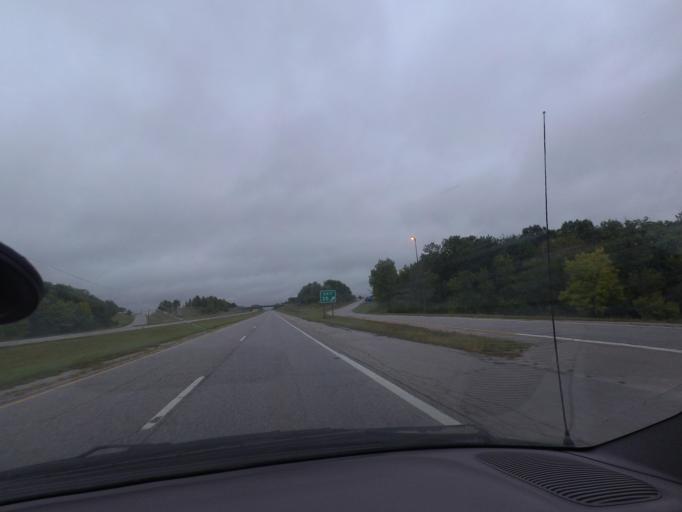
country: US
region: Illinois
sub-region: Pike County
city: Griggsville
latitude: 39.6739
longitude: -90.7738
